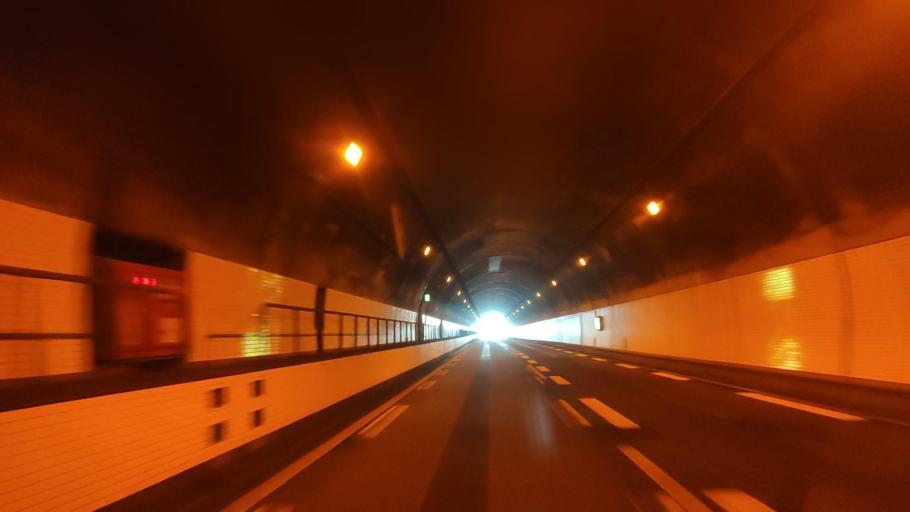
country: JP
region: Niigata
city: Itoigawa
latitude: 37.0217
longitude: 137.8410
